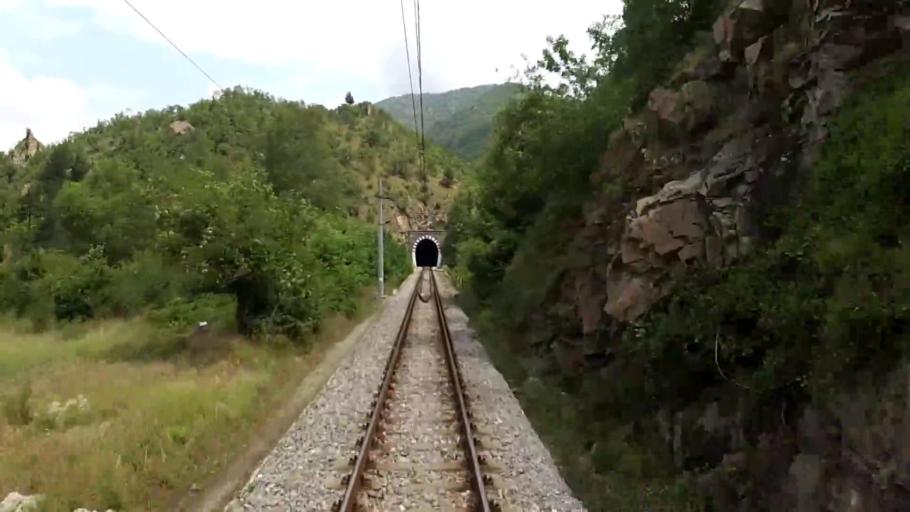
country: BG
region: Blagoevgrad
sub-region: Obshtina Kresna
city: Stara Kresna
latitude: 41.8239
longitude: 23.1591
